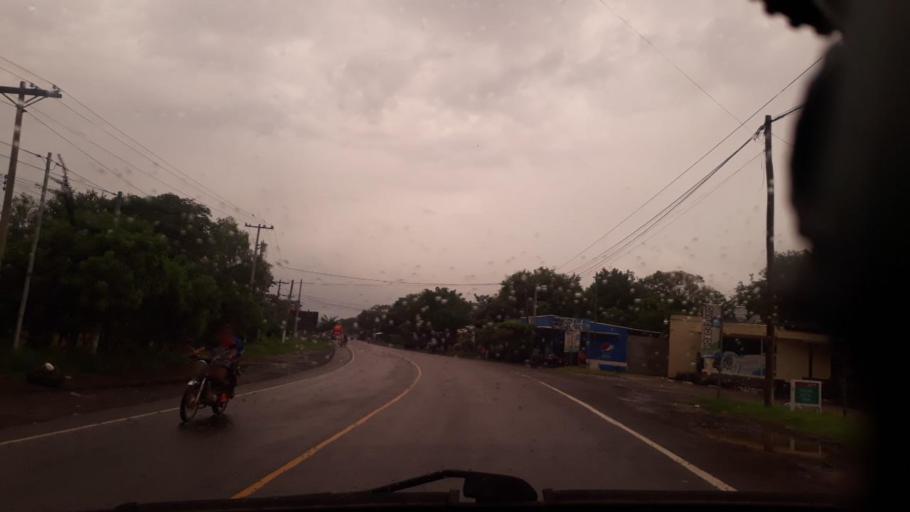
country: SV
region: Ahuachapan
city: San Francisco Menendez
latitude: 13.8809
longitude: -90.0993
